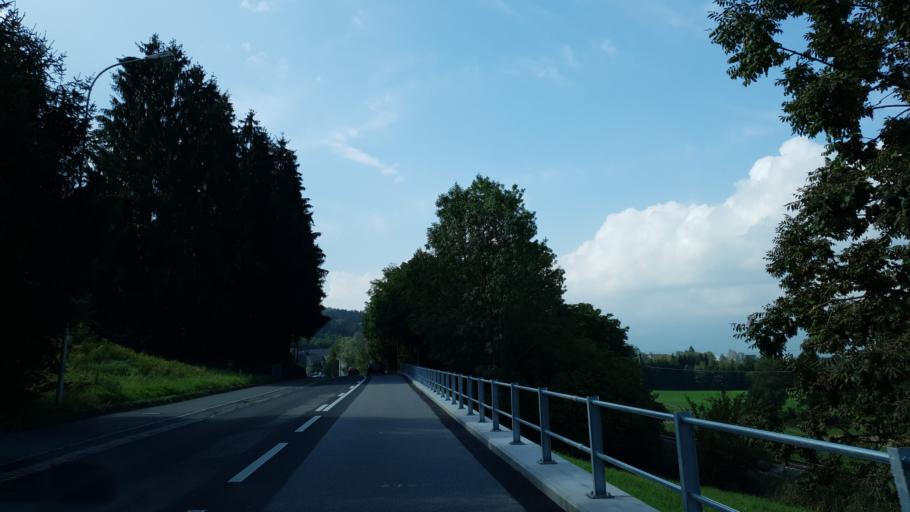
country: LI
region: Mauren
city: Mauren
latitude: 47.2148
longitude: 9.5649
